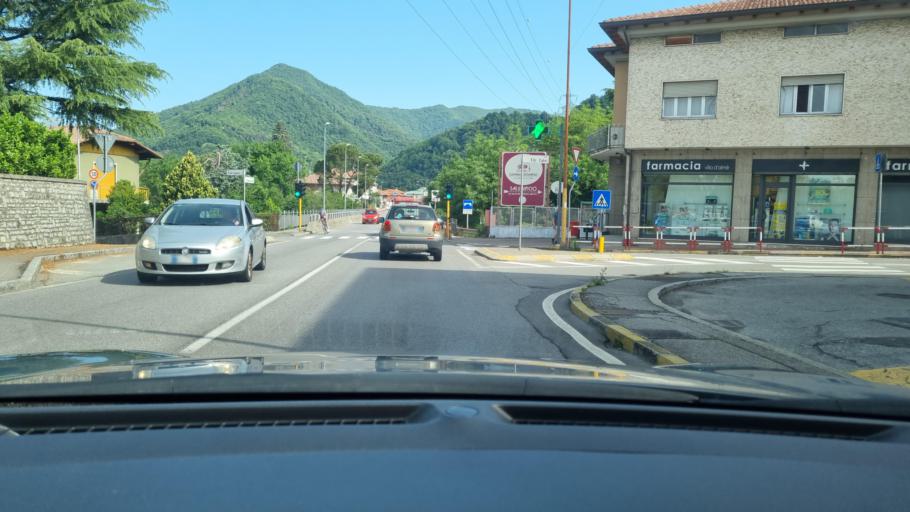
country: IT
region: Lombardy
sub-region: Provincia di Bergamo
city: Villa d'Alme
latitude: 45.7504
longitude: 9.6121
